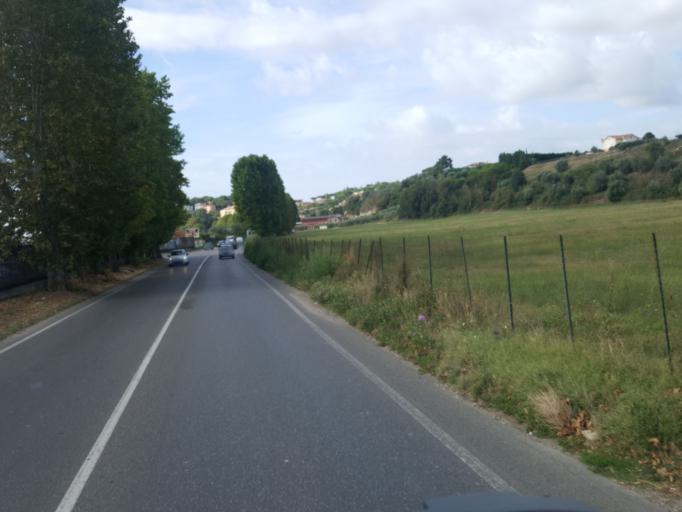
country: IT
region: Latium
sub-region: Citta metropolitana di Roma Capitale
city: Bivio di Capanelle
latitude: 42.1126
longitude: 12.5863
